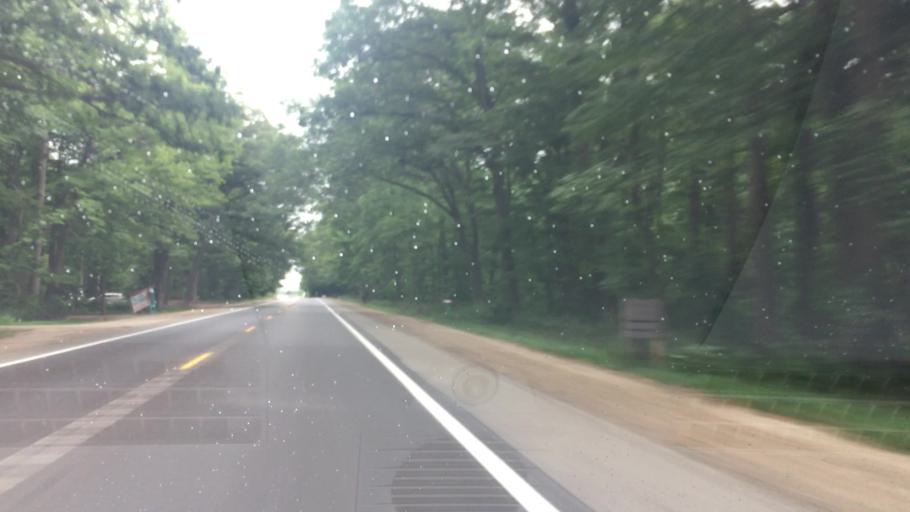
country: US
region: Michigan
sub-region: Ottawa County
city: Spring Lake
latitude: 42.9722
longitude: -86.1403
